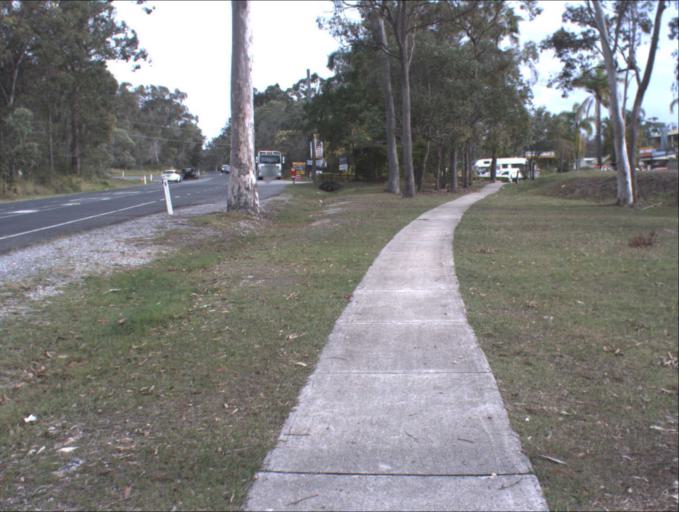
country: AU
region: Queensland
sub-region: Logan
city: Logan Reserve
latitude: -27.7224
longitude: 153.0903
